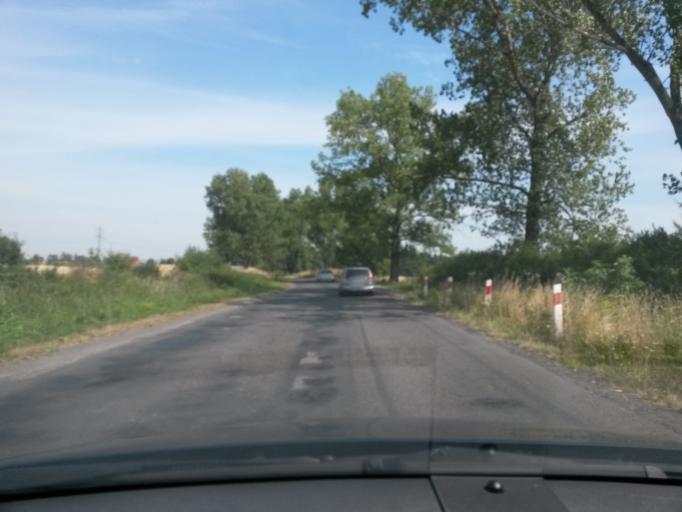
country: PL
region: Lower Silesian Voivodeship
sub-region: Powiat legnicki
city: Legnickie Pole
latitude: 51.1310
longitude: 16.3422
